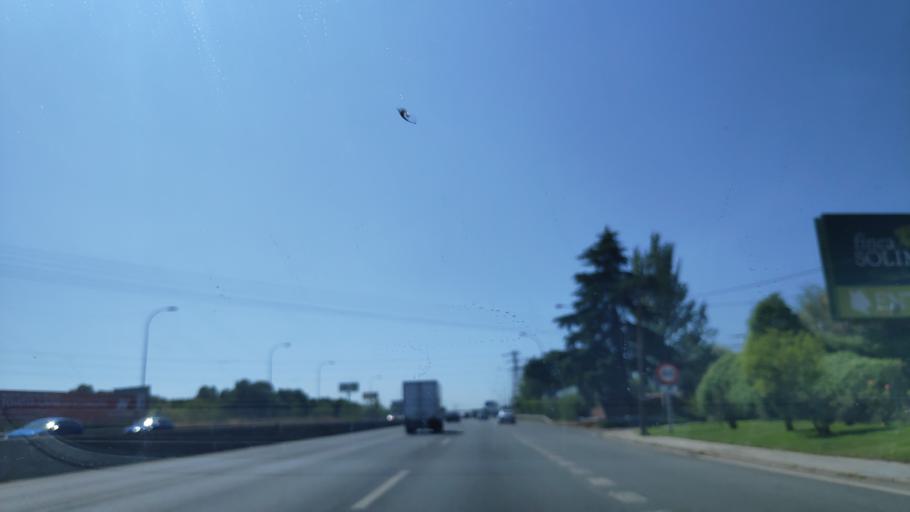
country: ES
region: Madrid
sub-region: Provincia de Madrid
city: Villaverde
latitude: 40.3494
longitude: -3.7229
